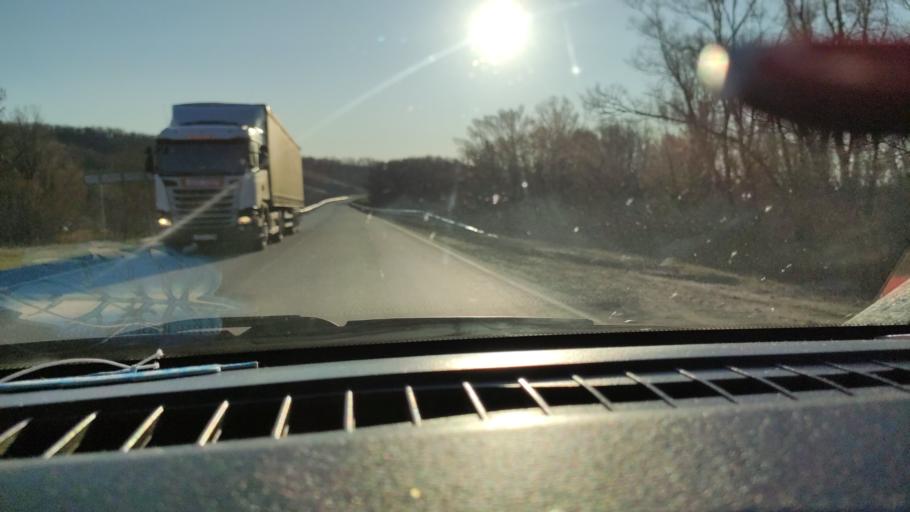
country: RU
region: Saratov
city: Tersa
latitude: 52.1033
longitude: 47.4810
